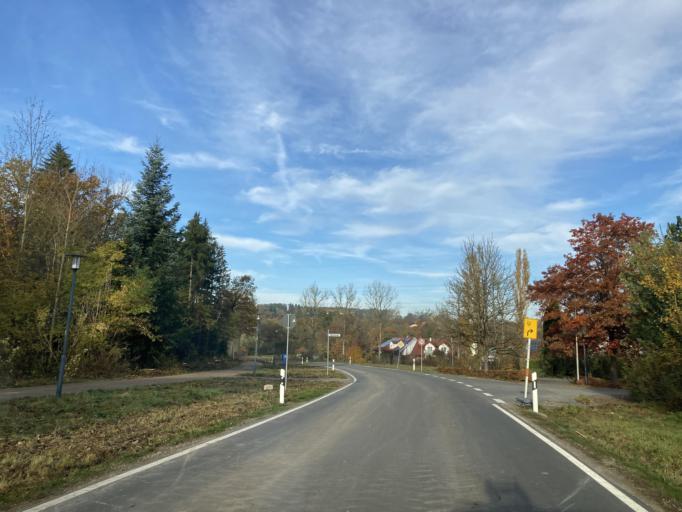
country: DE
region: Baden-Wuerttemberg
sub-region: Tuebingen Region
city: Ofterdingen
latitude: 48.3993
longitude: 9.0242
